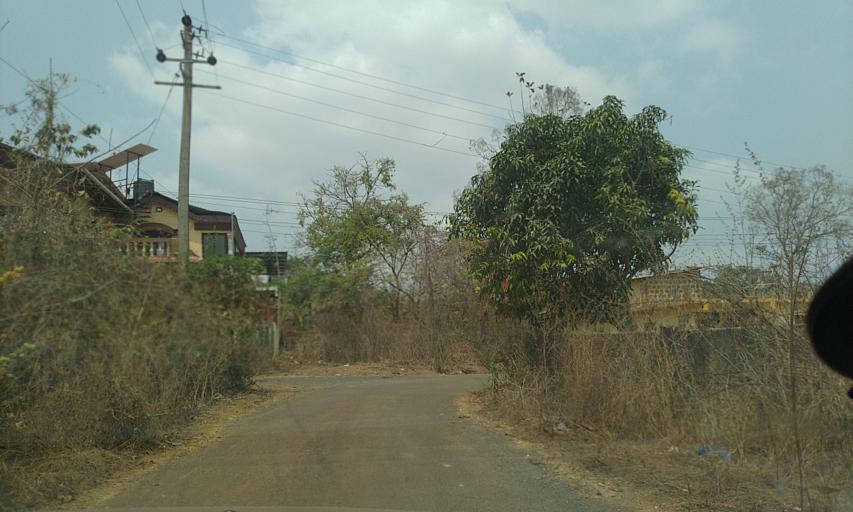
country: IN
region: Goa
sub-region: North Goa
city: Goa Velha
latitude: 15.4841
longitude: 73.9109
